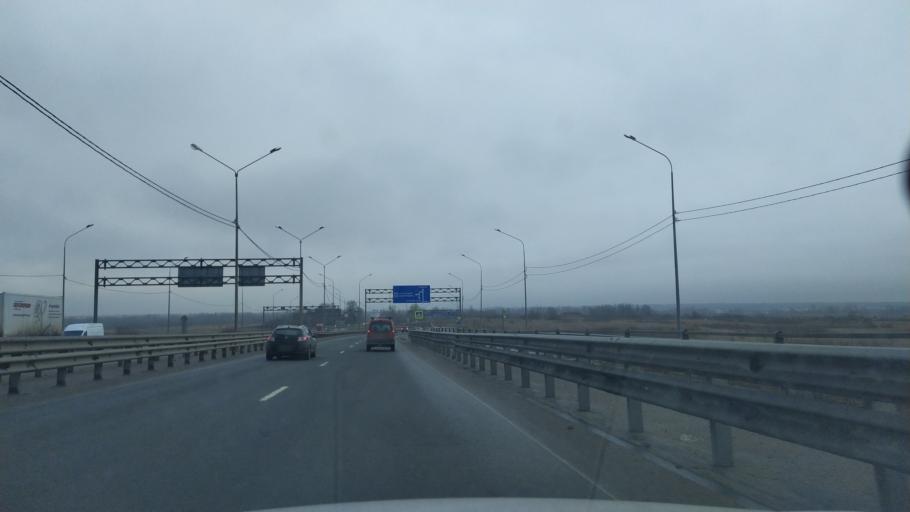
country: RU
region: St.-Petersburg
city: Aleksandrovskaya
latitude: 59.7173
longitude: 30.2867
